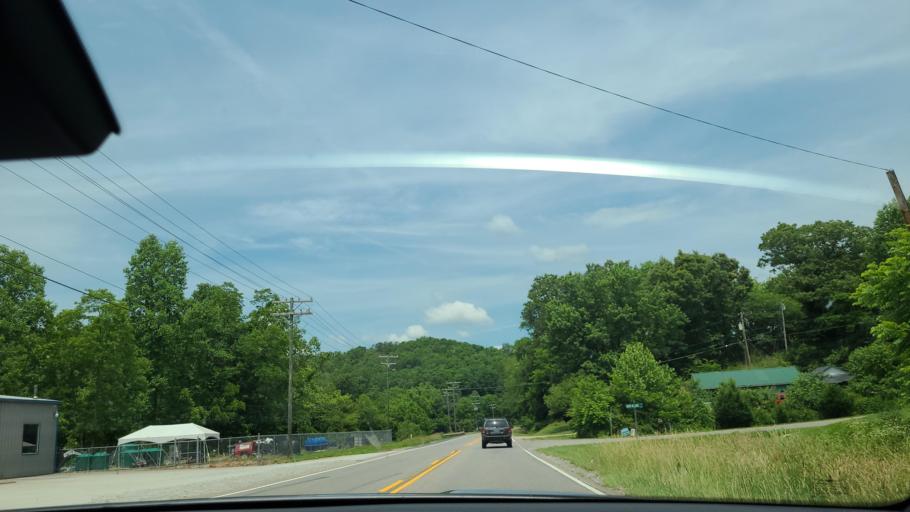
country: US
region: North Carolina
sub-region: Macon County
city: Franklin
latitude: 35.1689
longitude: -83.3372
